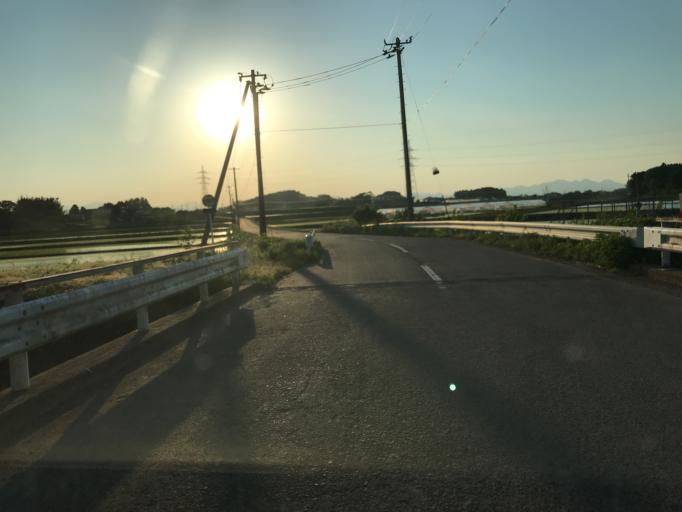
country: JP
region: Fukushima
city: Ishikawa
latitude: 37.1773
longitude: 140.3412
